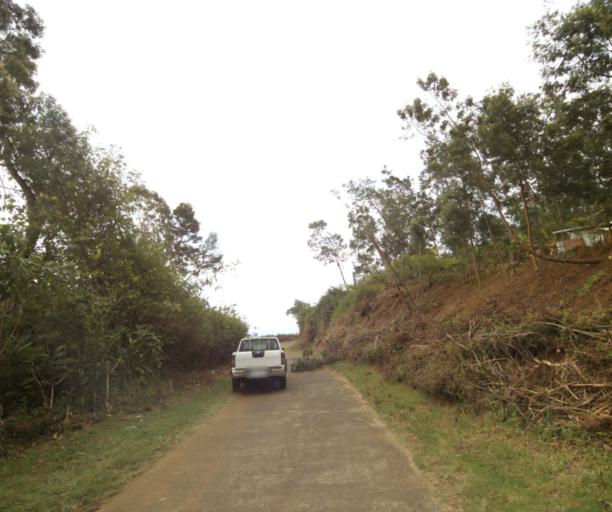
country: RE
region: Reunion
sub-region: Reunion
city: Saint-Paul
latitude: -21.0132
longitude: 55.3483
